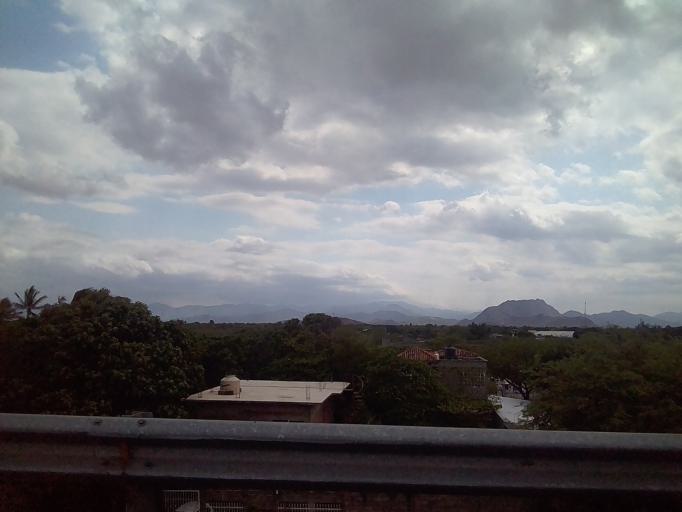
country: MX
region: Oaxaca
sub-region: Santo Domingo Tehuantepec
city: Santo Domingo Tehuantepec
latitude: 16.3197
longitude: -95.2390
